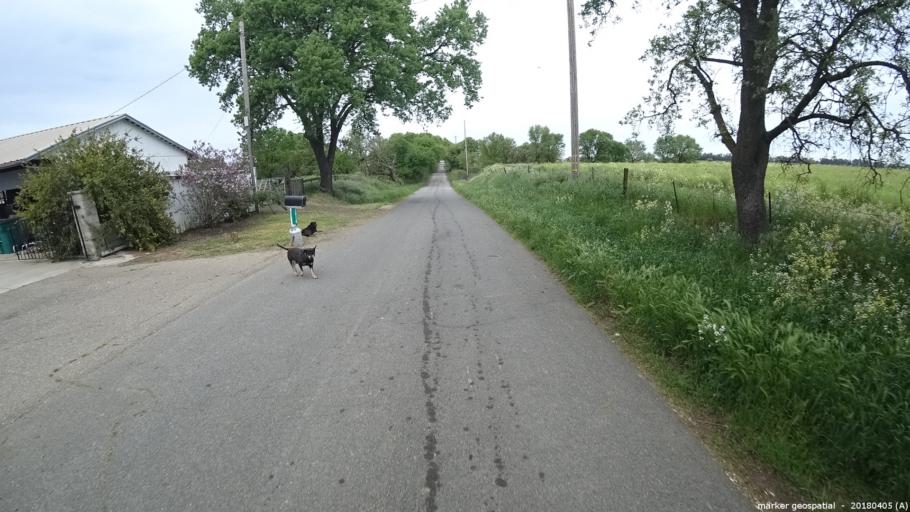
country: US
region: California
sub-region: Sacramento County
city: Galt
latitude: 38.2792
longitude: -121.3513
